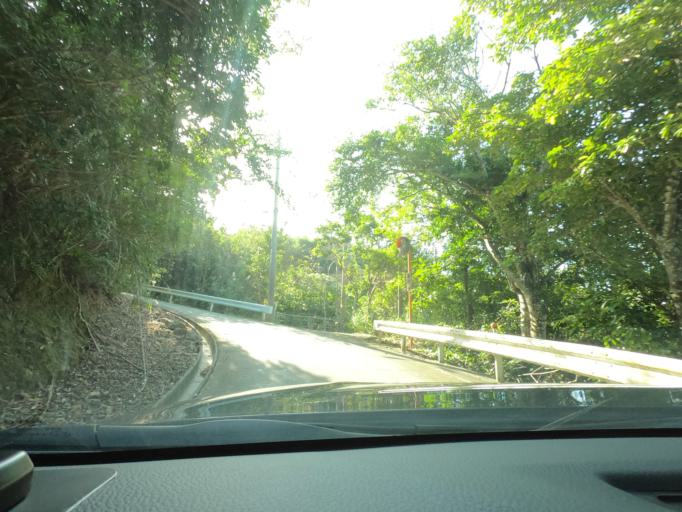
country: JP
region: Okinawa
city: Nago
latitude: 26.7563
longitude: 128.1987
